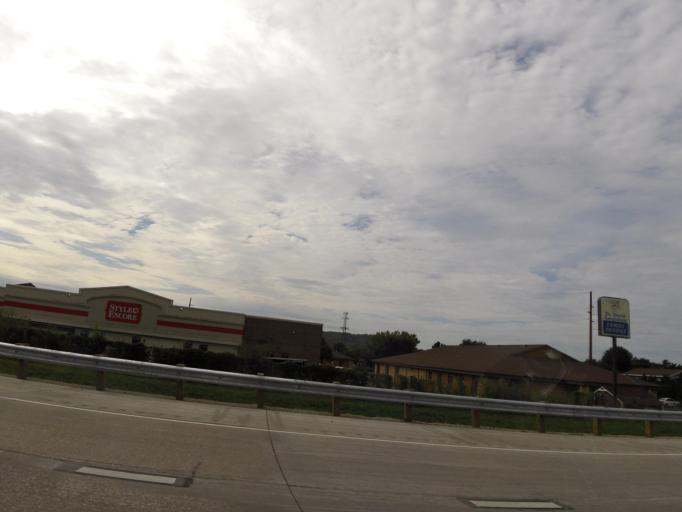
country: US
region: Wisconsin
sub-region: La Crosse County
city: Onalaska
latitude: 43.8770
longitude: -91.1974
